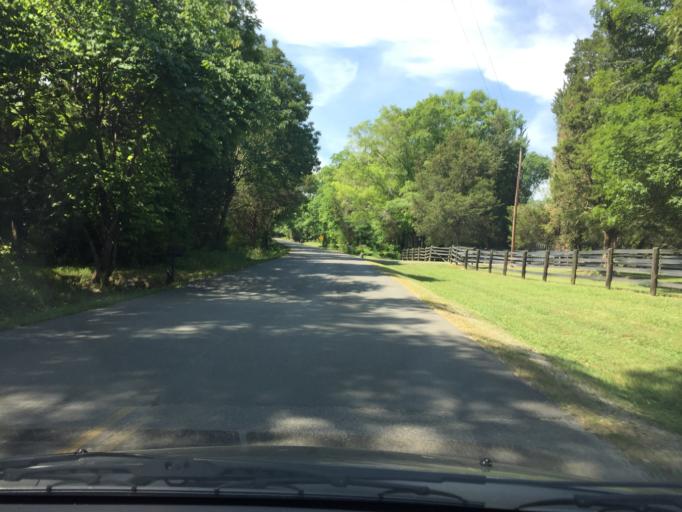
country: US
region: Tennessee
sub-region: Hamilton County
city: Collegedale
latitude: 35.1162
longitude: -85.0014
